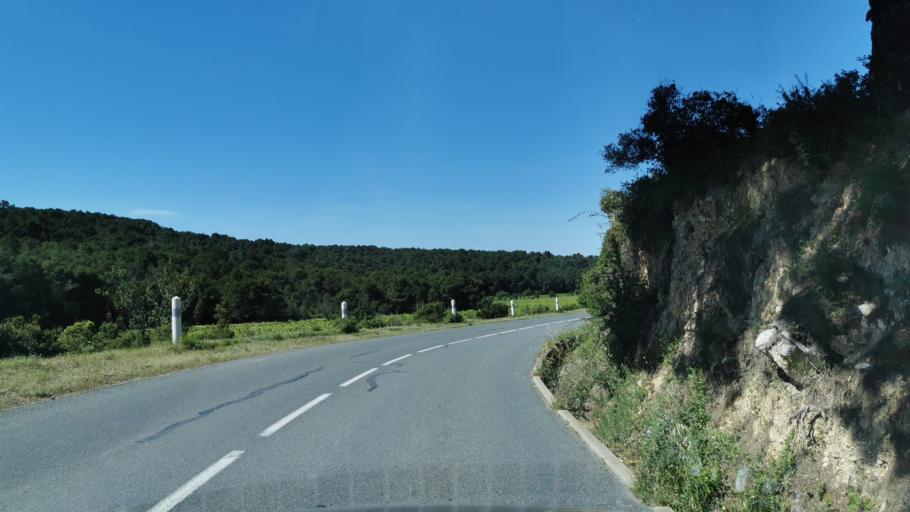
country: FR
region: Languedoc-Roussillon
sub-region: Departement de l'Aude
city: Armissan
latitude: 43.1725
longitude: 3.0760
